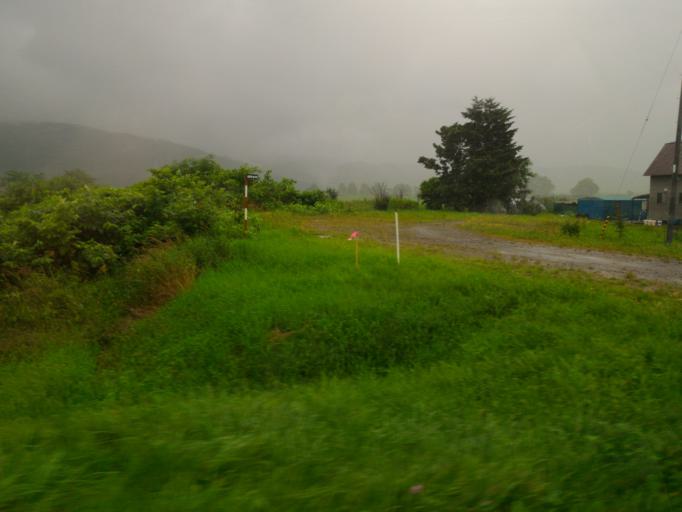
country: JP
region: Hokkaido
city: Makubetsu
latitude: 44.8580
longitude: 142.0544
